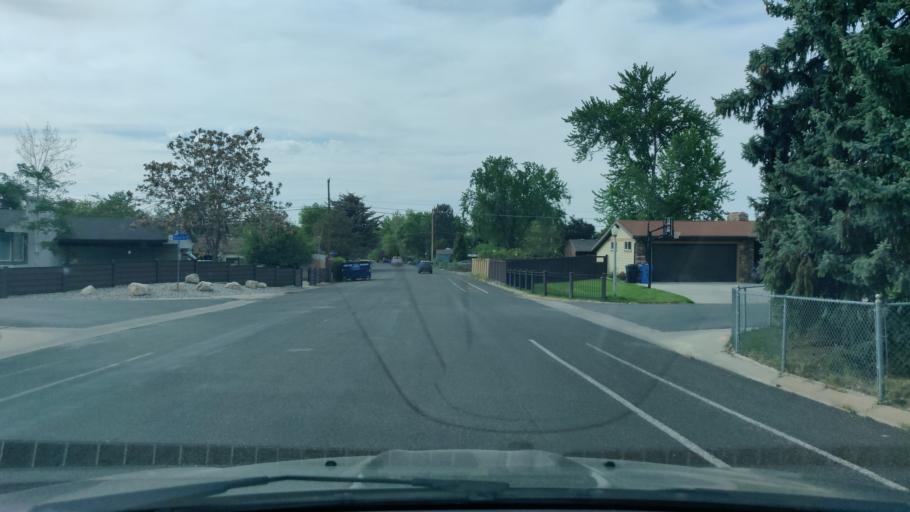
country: US
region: Utah
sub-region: Salt Lake County
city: Little Cottonwood Creek Valley
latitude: 40.6282
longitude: -111.8379
